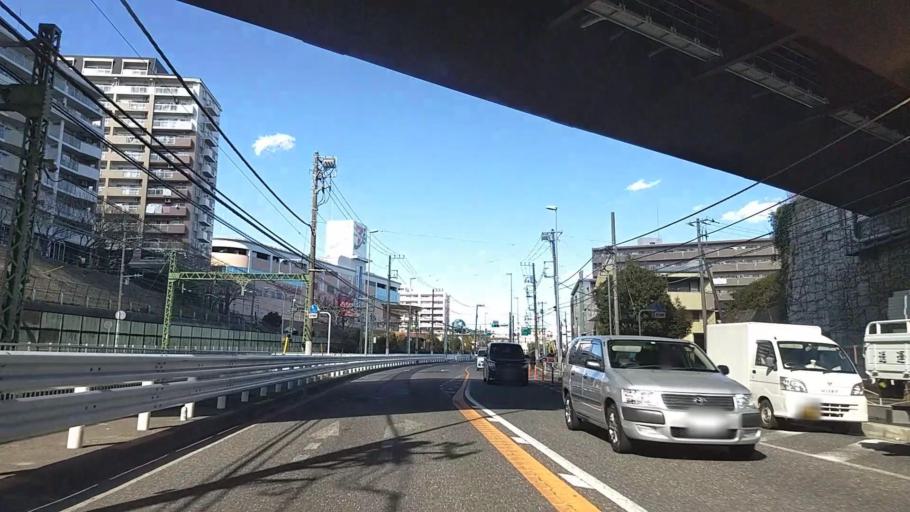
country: JP
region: Kanagawa
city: Zushi
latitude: 35.3566
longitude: 139.6280
